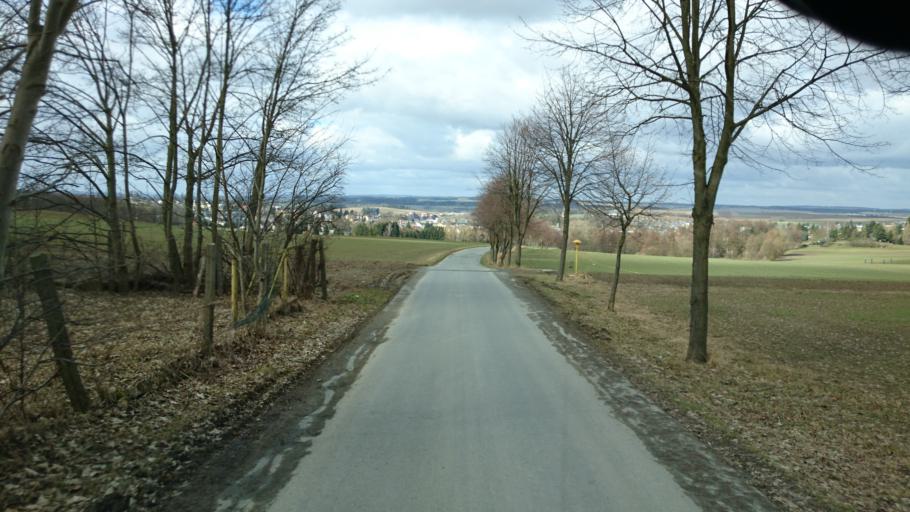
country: DE
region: Thuringia
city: Schleiz
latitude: 50.5678
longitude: 11.8255
